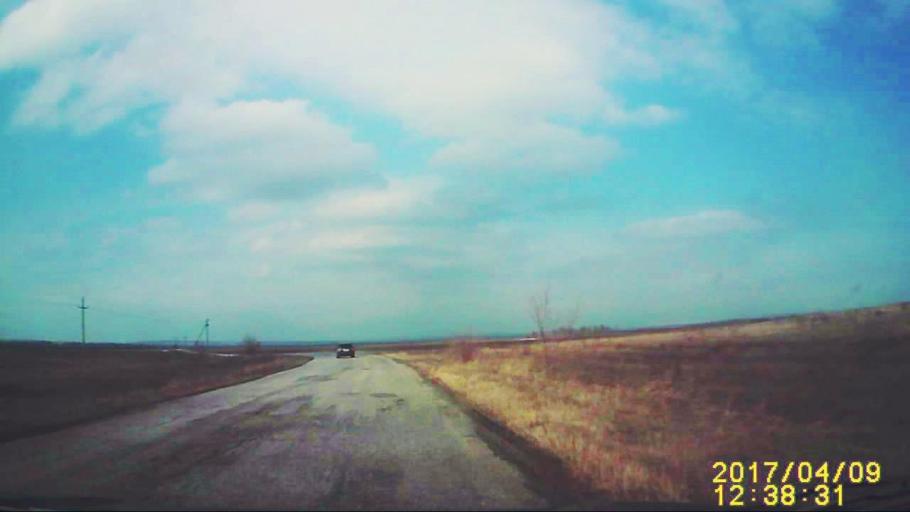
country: RU
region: Ulyanovsk
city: Ignatovka
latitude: 53.9945
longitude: 47.9662
